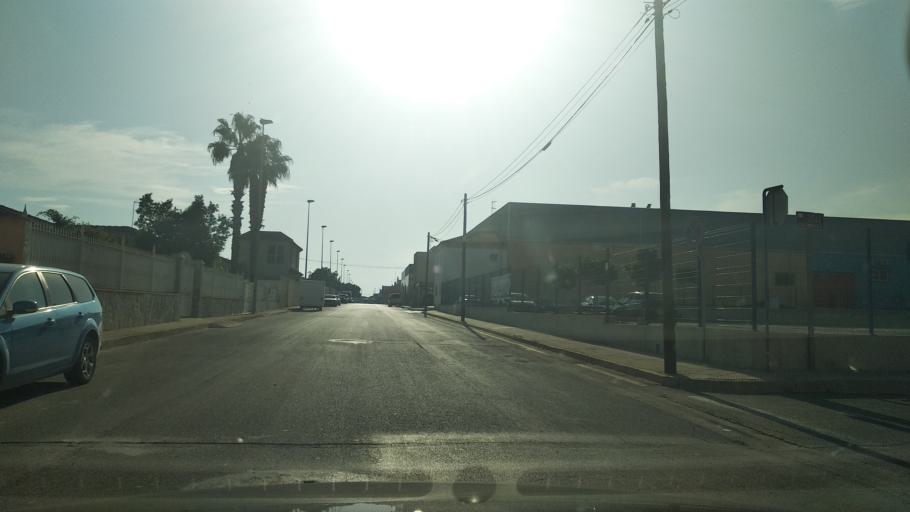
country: ES
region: Murcia
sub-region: Murcia
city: San Javier
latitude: 37.8100
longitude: -0.8391
